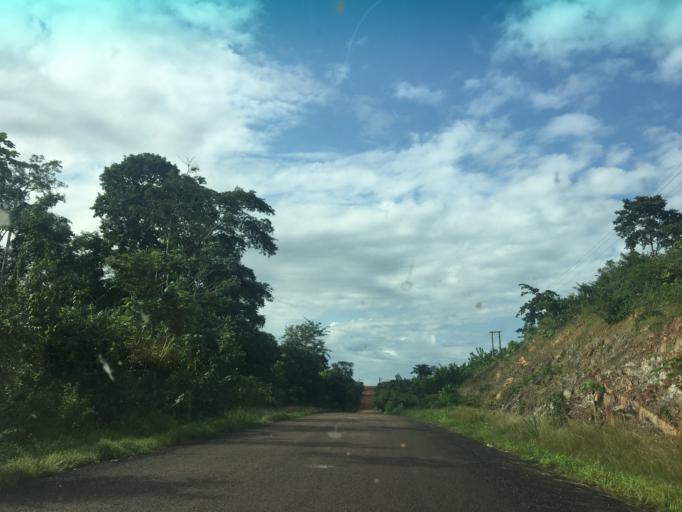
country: GH
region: Western
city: Wassa-Akropong
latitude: 5.9776
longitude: -2.4157
